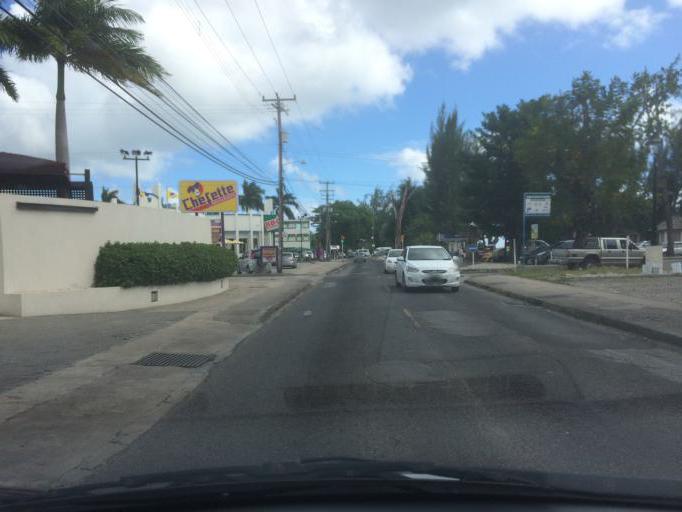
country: BB
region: Saint Michael
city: Bridgetown
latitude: 13.0746
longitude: -59.5891
